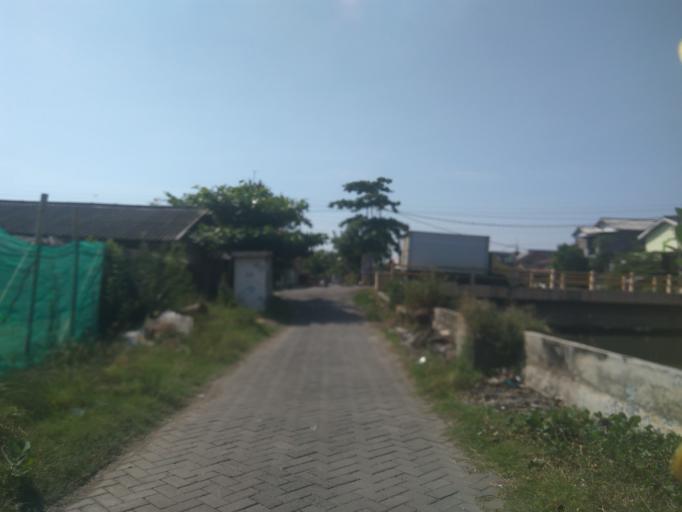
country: ID
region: Central Java
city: Semarang
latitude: -6.9628
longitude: 110.4408
